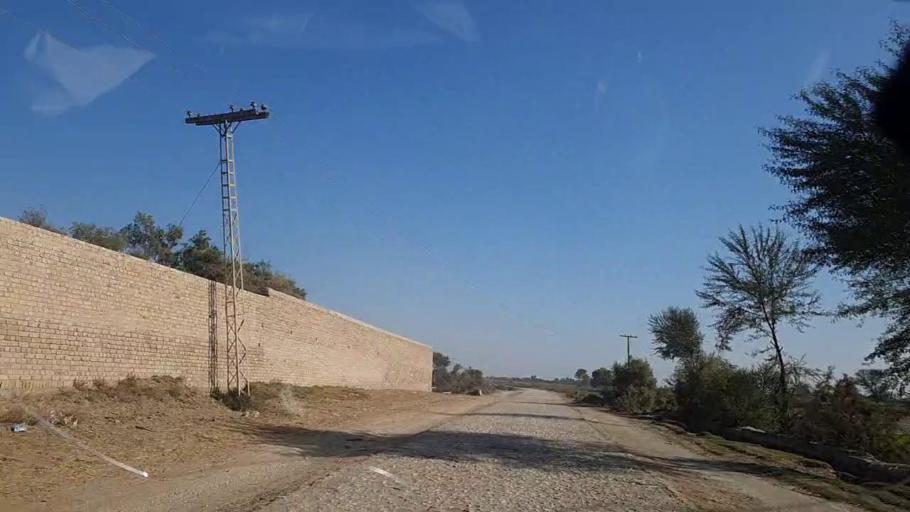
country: PK
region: Sindh
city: Khanpur
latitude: 27.8038
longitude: 69.3708
